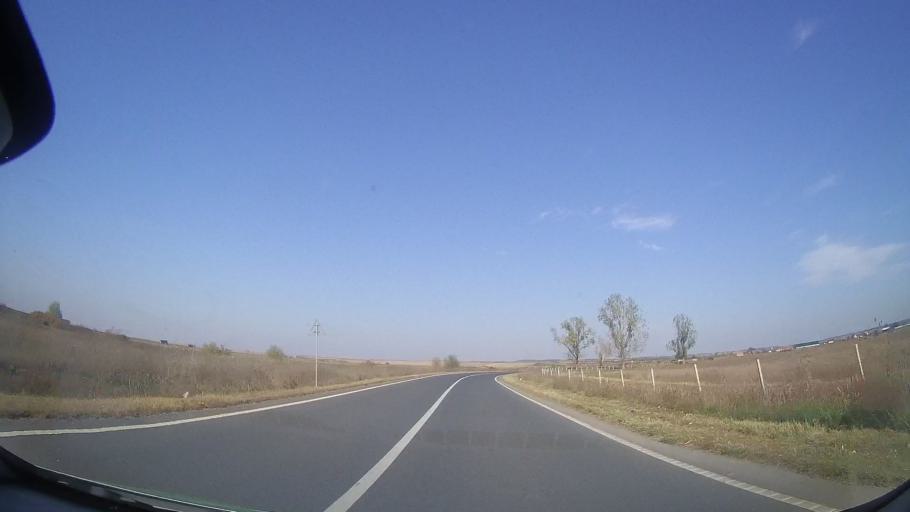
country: RO
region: Timis
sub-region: Comuna Belint
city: Belint
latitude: 45.7834
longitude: 21.7326
